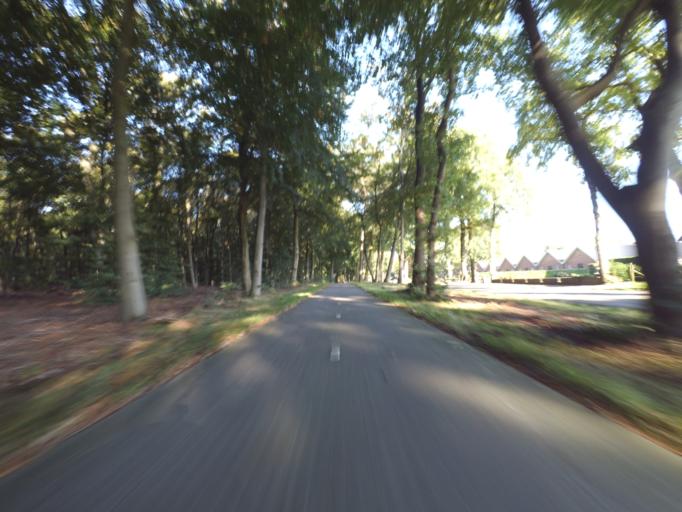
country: NL
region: Gelderland
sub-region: Gemeente Barneveld
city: Garderen
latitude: 52.2565
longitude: 5.7096
